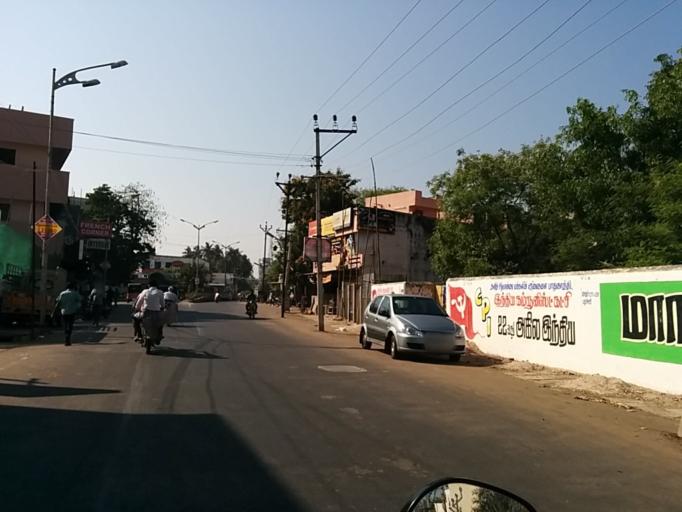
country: IN
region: Pondicherry
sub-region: Puducherry
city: Puducherry
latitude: 11.9519
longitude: 79.8303
